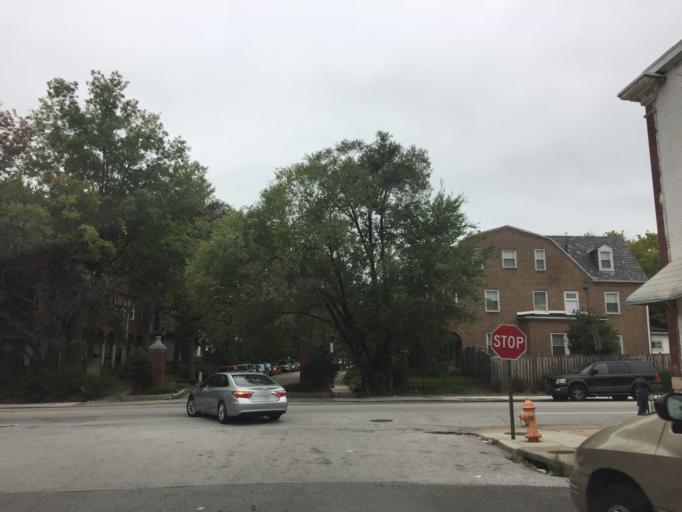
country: US
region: Maryland
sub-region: City of Baltimore
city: Baltimore
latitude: 39.3309
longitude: -76.6092
